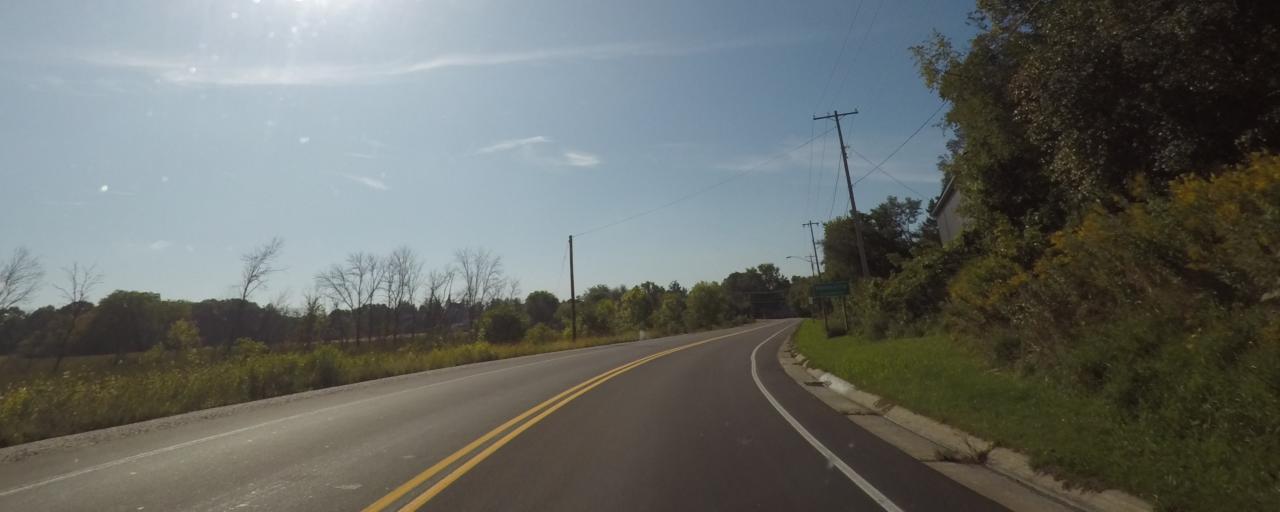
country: US
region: Wisconsin
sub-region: Jefferson County
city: Johnson Creek
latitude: 43.0156
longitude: -88.7056
